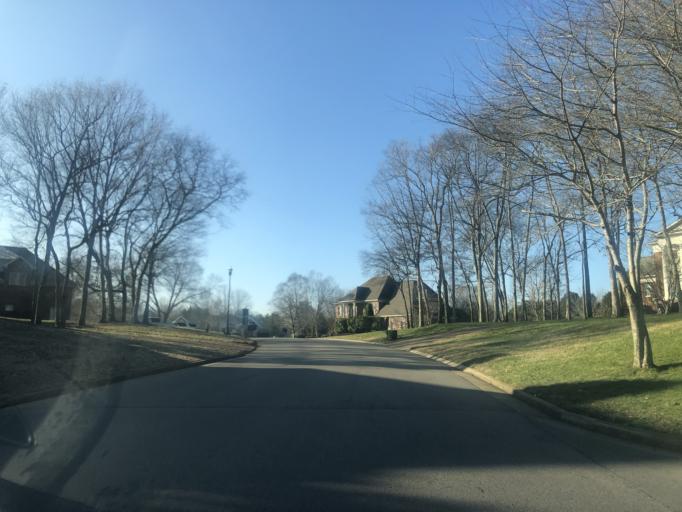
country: US
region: Tennessee
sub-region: Williamson County
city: Brentwood Estates
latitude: 35.9914
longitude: -86.7248
